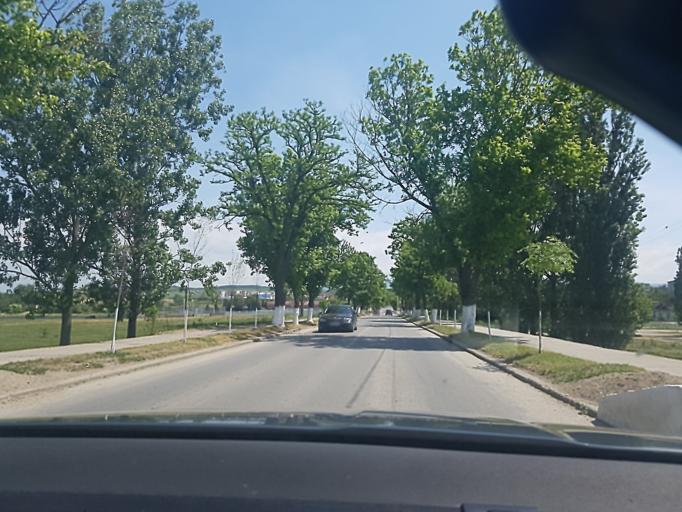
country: RO
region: Hunedoara
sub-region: Comuna Calan
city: Calan
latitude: 45.7343
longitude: 23.0158
